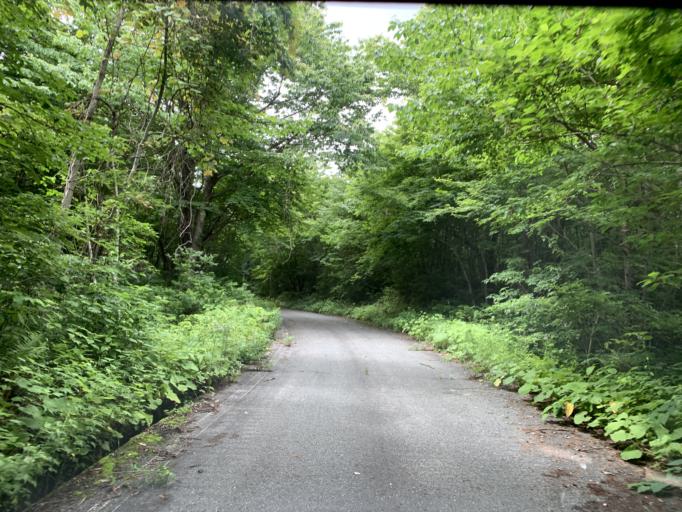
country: JP
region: Iwate
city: Ichinoseki
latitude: 38.9326
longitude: 140.8916
